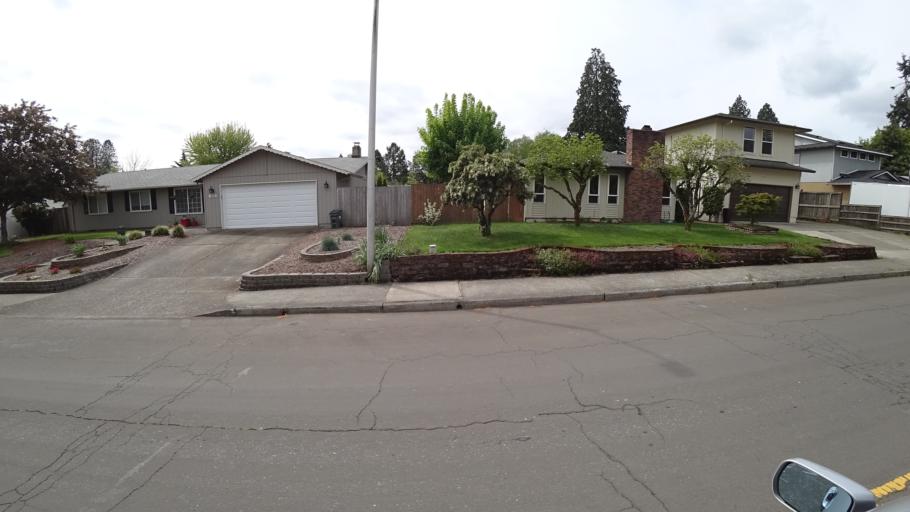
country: US
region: Oregon
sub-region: Washington County
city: Hillsboro
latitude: 45.5299
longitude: -122.9951
